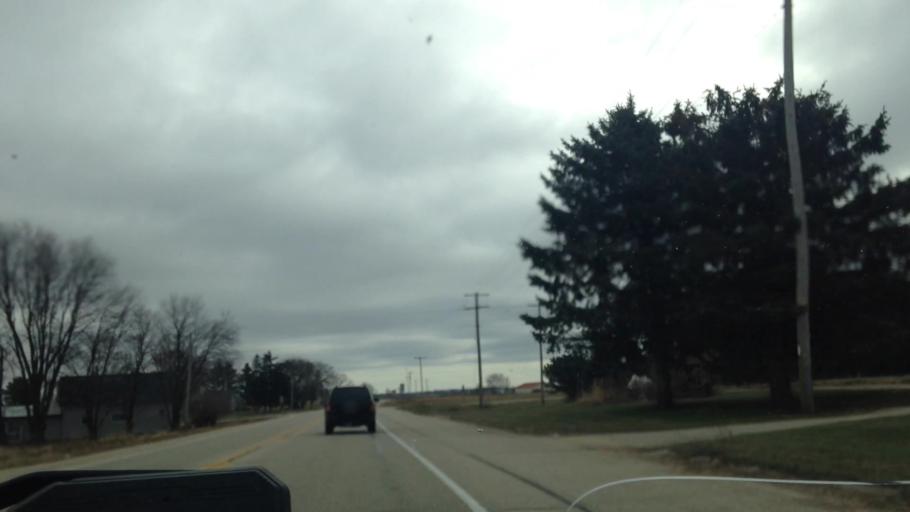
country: US
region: Wisconsin
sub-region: Dodge County
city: Theresa
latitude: 43.4252
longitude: -88.4222
